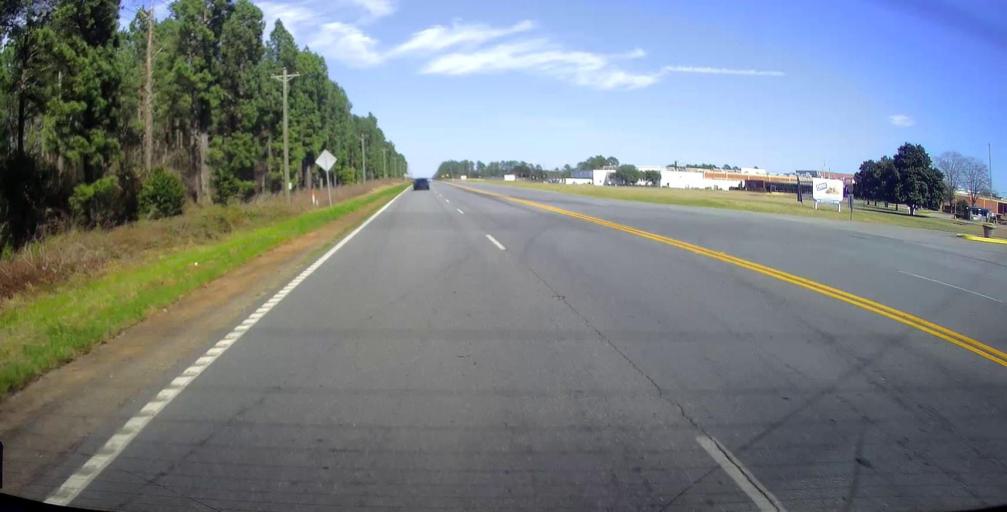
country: US
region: Georgia
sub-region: Houston County
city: Perry
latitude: 32.4421
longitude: -83.6339
